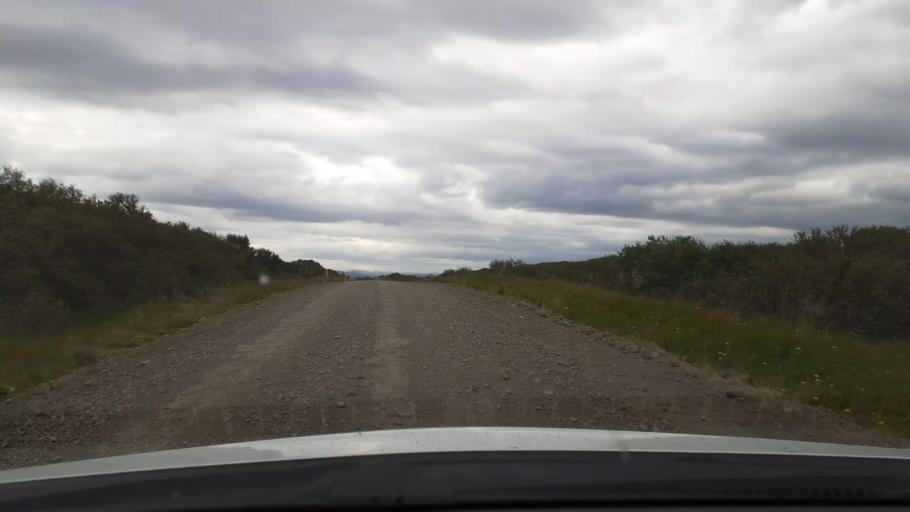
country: IS
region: West
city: Borgarnes
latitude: 64.6020
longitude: -21.9715
